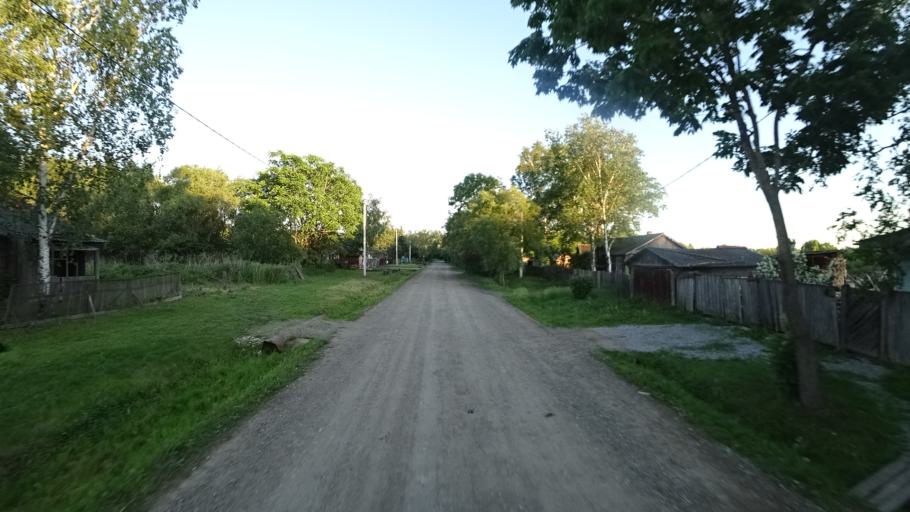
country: RU
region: Khabarovsk Krai
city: Khor
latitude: 47.8514
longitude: 134.9834
